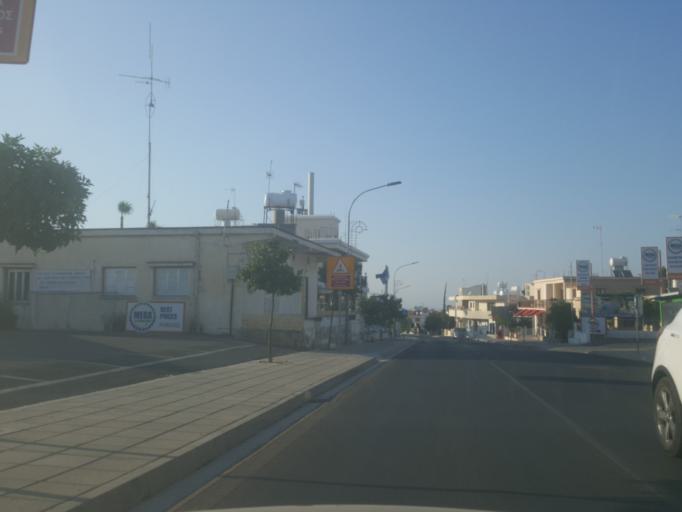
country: CY
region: Ammochostos
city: Deryneia
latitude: 35.0661
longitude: 33.9609
